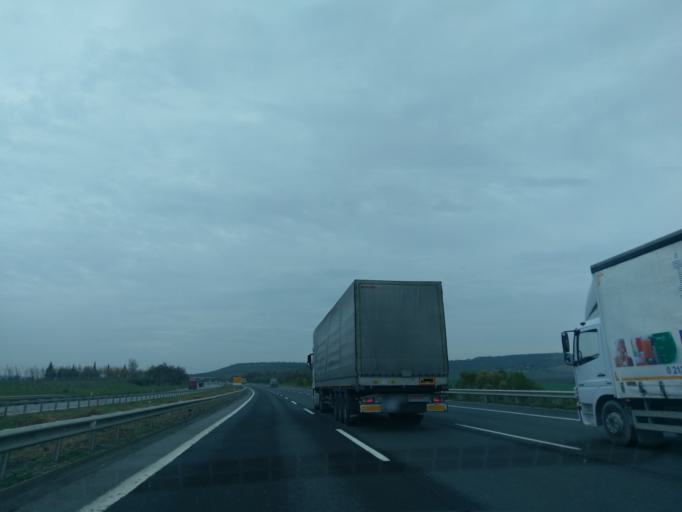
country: TR
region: Istanbul
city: Canta
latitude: 41.1550
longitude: 28.1421
